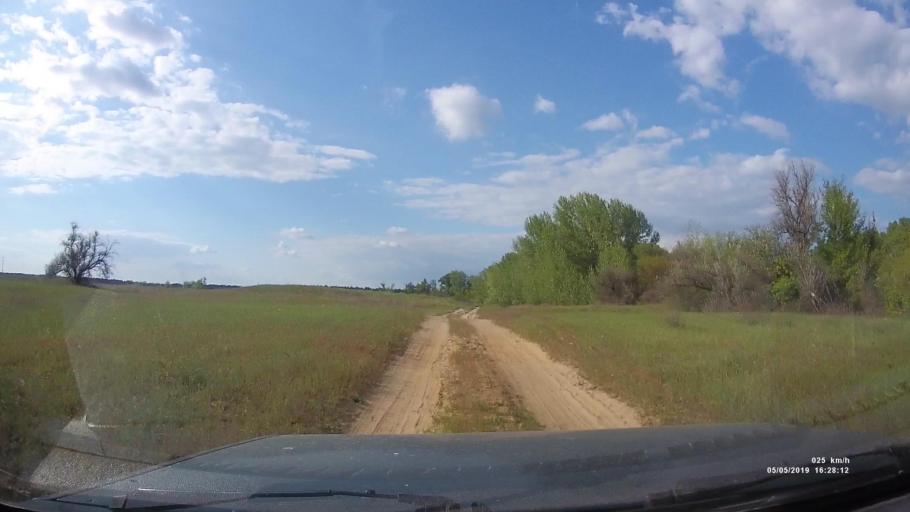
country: RU
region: Rostov
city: Ust'-Donetskiy
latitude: 47.7668
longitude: 41.0161
